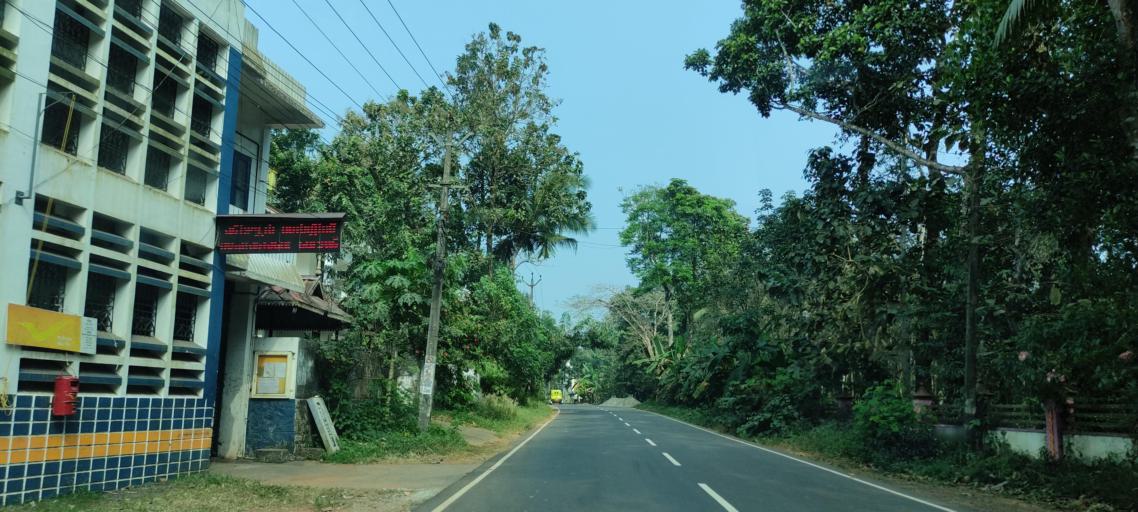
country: IN
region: Kerala
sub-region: Ernakulam
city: Piravam
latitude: 9.8032
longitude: 76.4824
